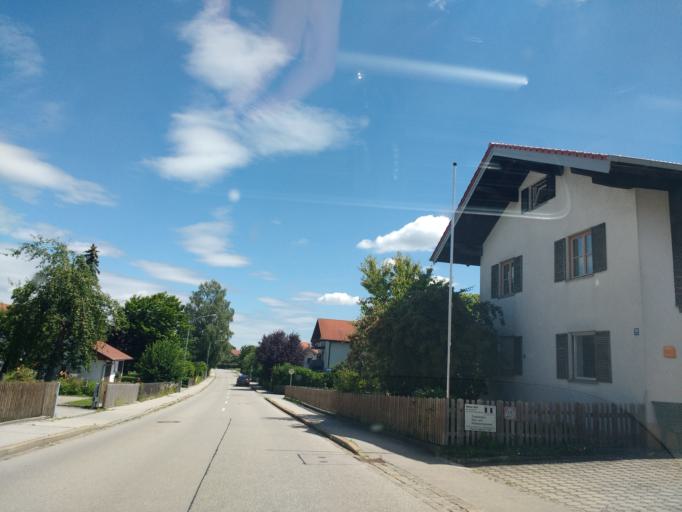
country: DE
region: Bavaria
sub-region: Upper Bavaria
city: Engelsberg
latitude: 48.1178
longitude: 12.5439
